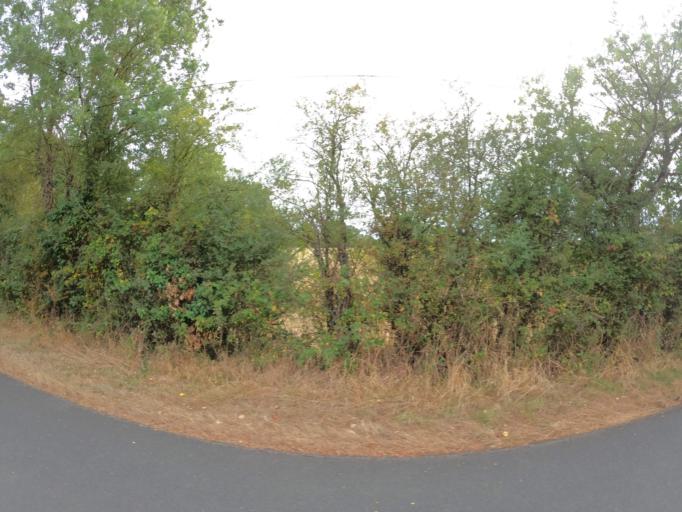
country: FR
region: Pays de la Loire
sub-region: Departement de Maine-et-Loire
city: Saint-Christophe-du-Bois
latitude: 47.0397
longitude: -0.9709
